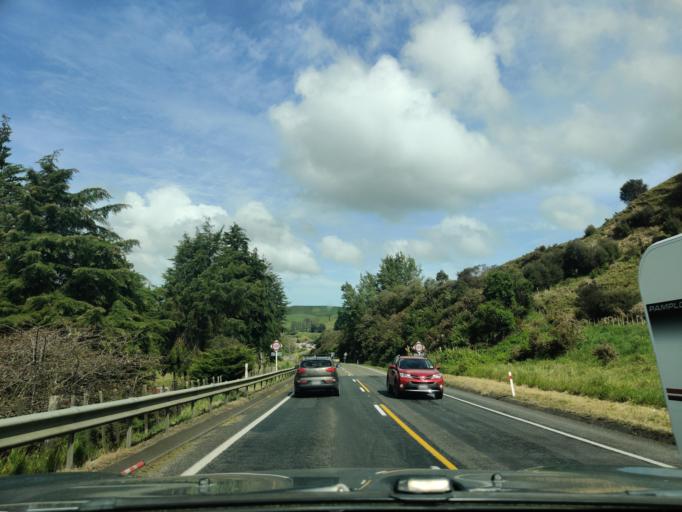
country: NZ
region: Manawatu-Wanganui
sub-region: Wanganui District
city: Wanganui
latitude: -39.8433
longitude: 174.9241
